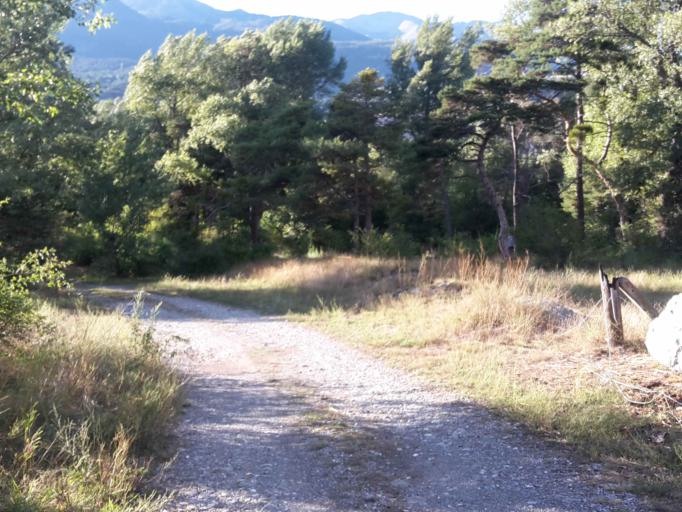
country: FR
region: Provence-Alpes-Cote d'Azur
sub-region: Departement des Hautes-Alpes
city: Embrun
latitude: 44.5538
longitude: 6.4886
